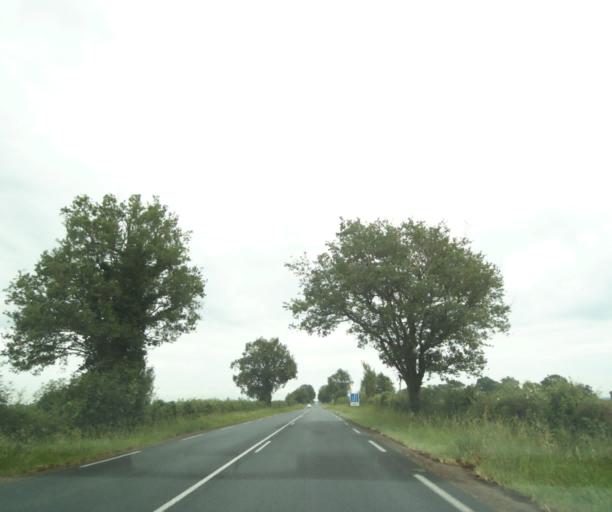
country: FR
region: Poitou-Charentes
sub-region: Departement des Deux-Sevres
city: Viennay
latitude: 46.7407
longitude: -0.2319
